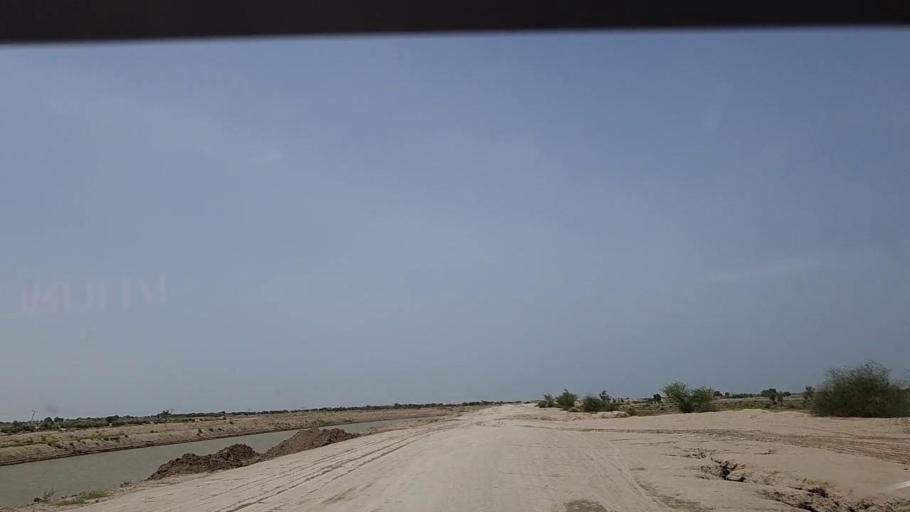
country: PK
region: Sindh
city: Johi
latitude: 26.7317
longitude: 67.6827
